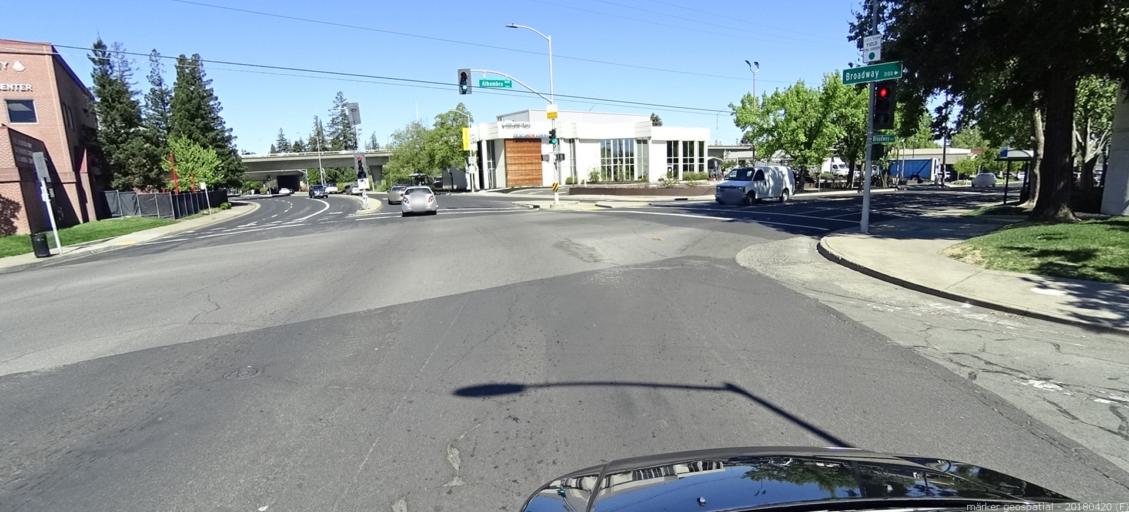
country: US
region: California
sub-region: Sacramento County
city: Sacramento
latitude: 38.5560
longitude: -121.4723
